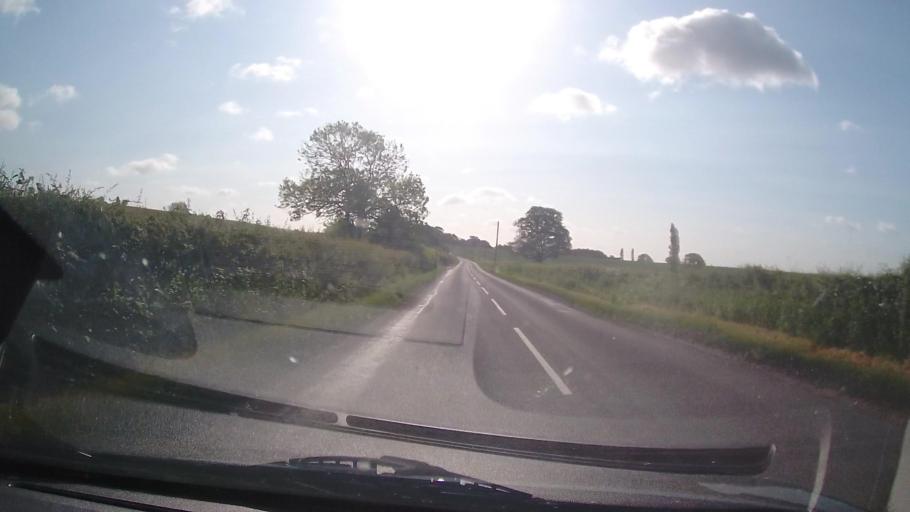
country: GB
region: England
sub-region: Shropshire
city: Withington
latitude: 52.7535
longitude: -2.5989
